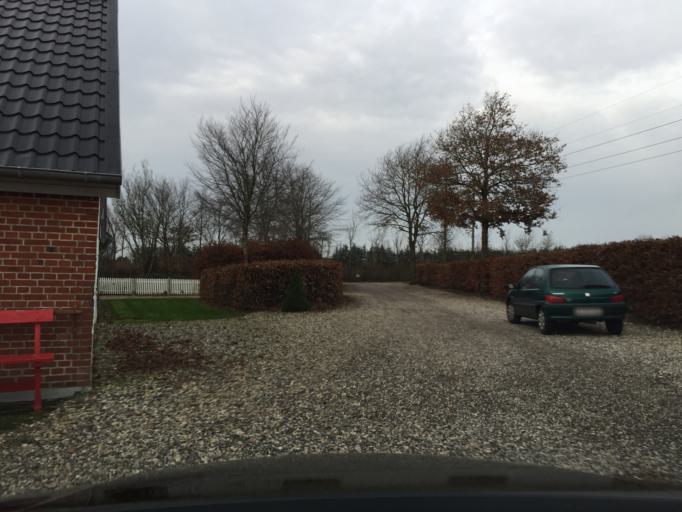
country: DK
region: Central Jutland
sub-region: Viborg Kommune
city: Bjerringbro
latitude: 56.3583
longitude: 9.5551
